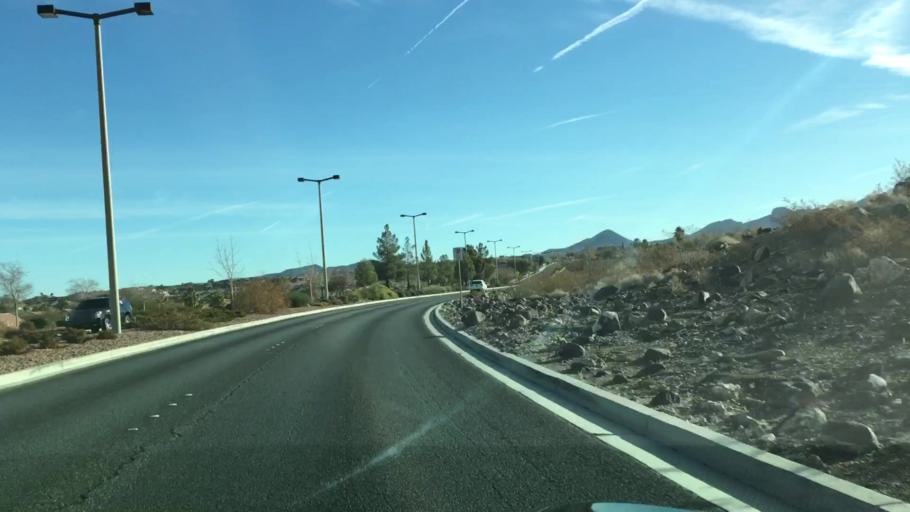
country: US
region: Nevada
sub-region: Clark County
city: Whitney
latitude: 35.9692
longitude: -115.1174
